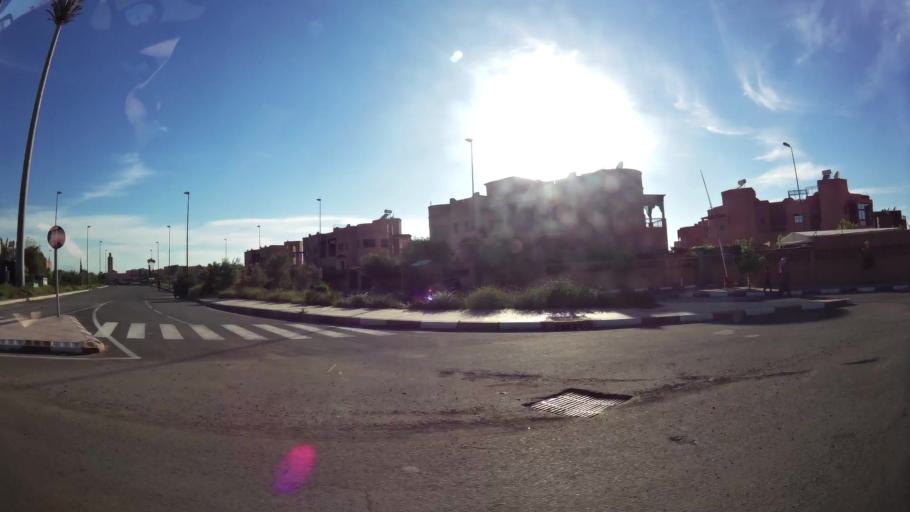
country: MA
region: Marrakech-Tensift-Al Haouz
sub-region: Marrakech
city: Marrakesh
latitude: 31.6753
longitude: -8.0591
